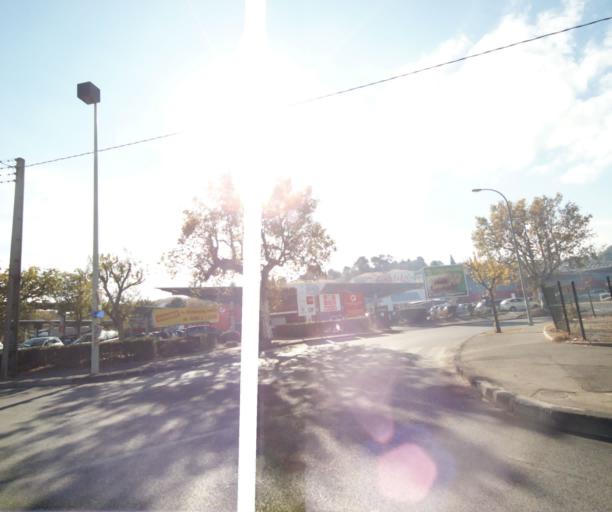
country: FR
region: Provence-Alpes-Cote d'Azur
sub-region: Departement des Bouches-du-Rhone
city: Plan-de-Cuques
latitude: 43.3350
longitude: 5.4532
